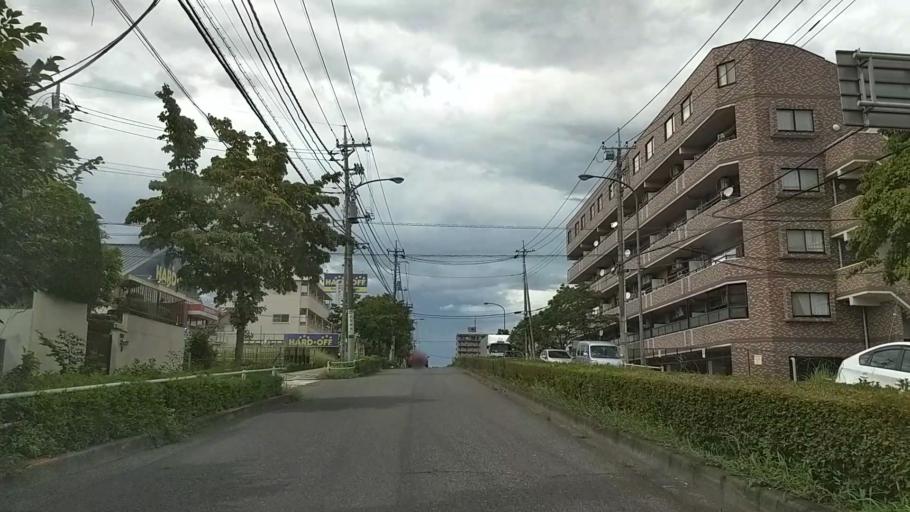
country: JP
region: Tokyo
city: Hachioji
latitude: 35.6389
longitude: 139.3090
